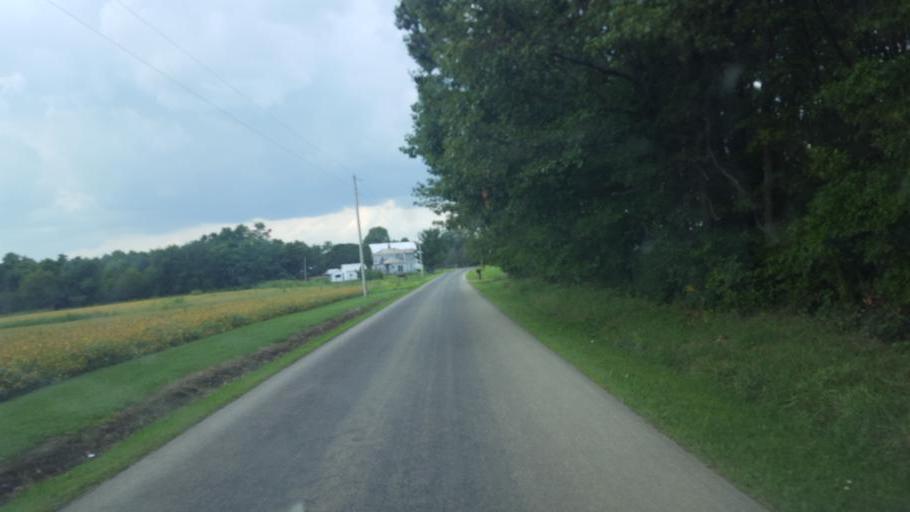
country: US
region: Ohio
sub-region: Knox County
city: Oak Hill
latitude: 40.3564
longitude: -82.3014
